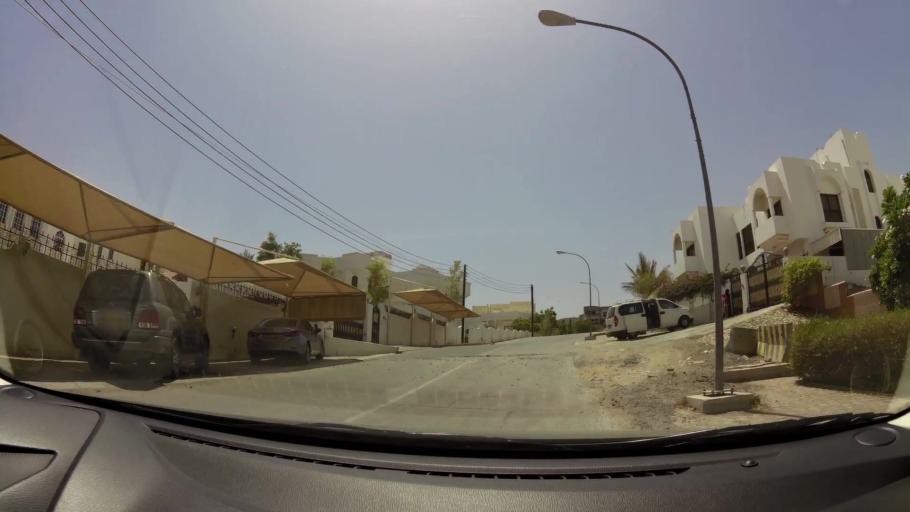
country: OM
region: Muhafazat Masqat
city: Bawshar
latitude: 23.5897
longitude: 58.4486
